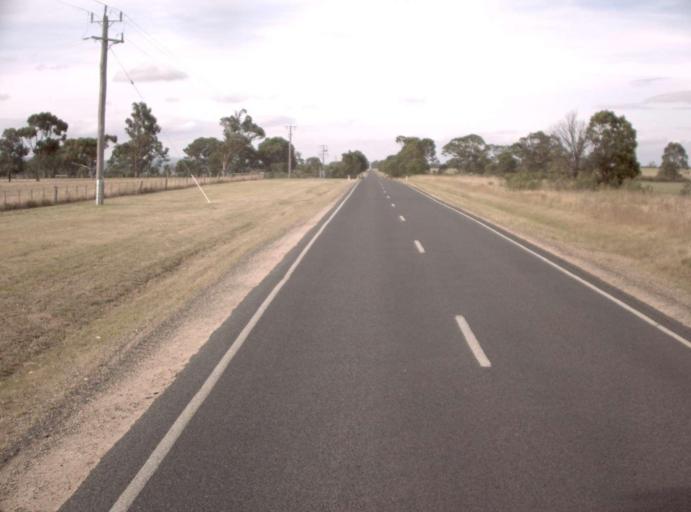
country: AU
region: Victoria
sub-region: Wellington
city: Heyfield
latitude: -38.0519
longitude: 146.6635
